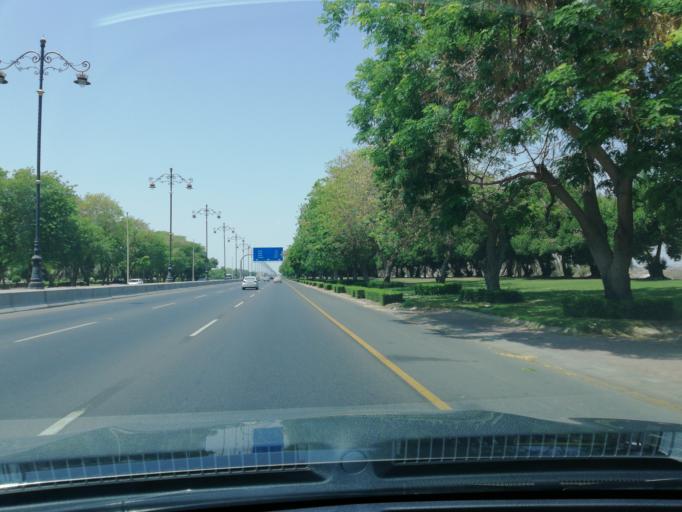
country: OM
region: Muhafazat Masqat
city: Bawshar
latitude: 23.5891
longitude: 58.3131
